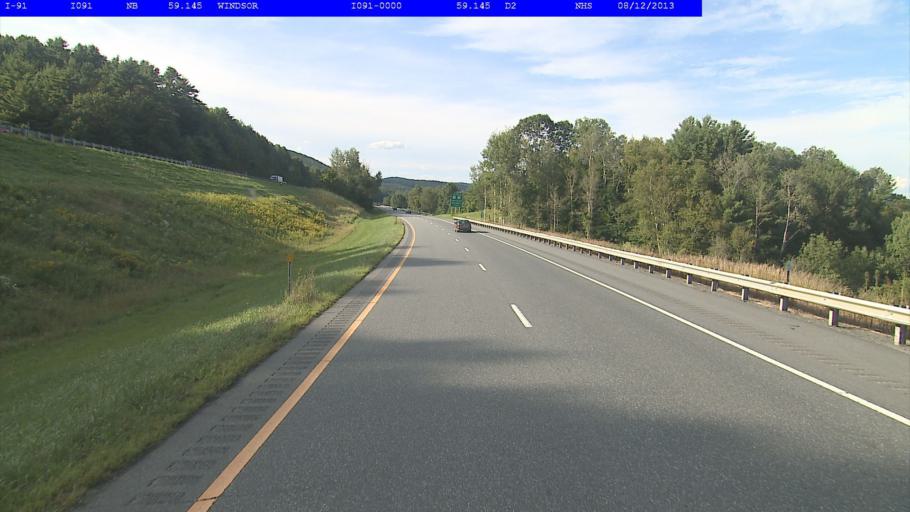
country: US
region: Vermont
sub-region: Windsor County
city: Windsor
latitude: 43.5105
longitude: -72.4059
